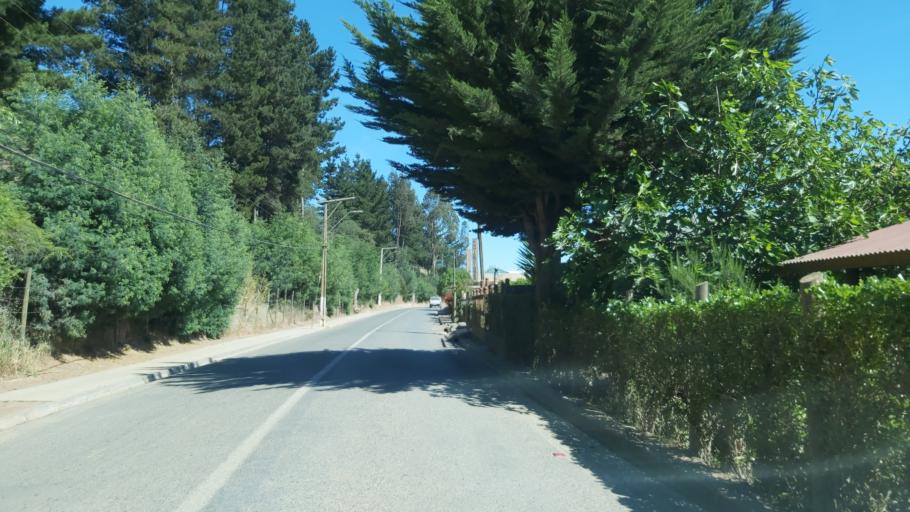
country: CL
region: Maule
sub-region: Provincia de Talca
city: Constitucion
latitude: -34.7734
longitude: -72.0655
